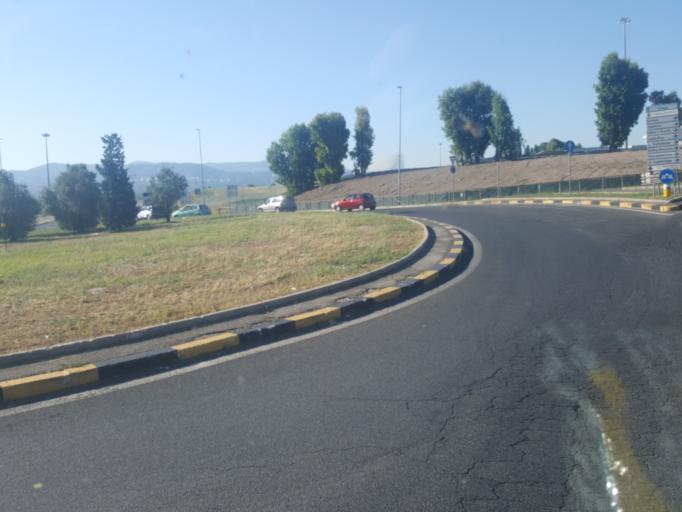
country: IT
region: Latium
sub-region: Citta metropolitana di Roma Capitale
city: Frascati
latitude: 41.8558
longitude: 12.6298
